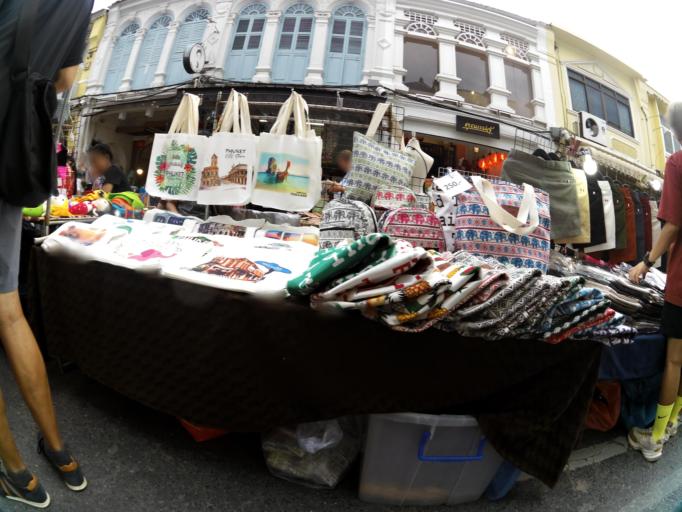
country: TH
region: Phuket
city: Ban Talat Nua
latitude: 7.8847
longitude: 98.3896
